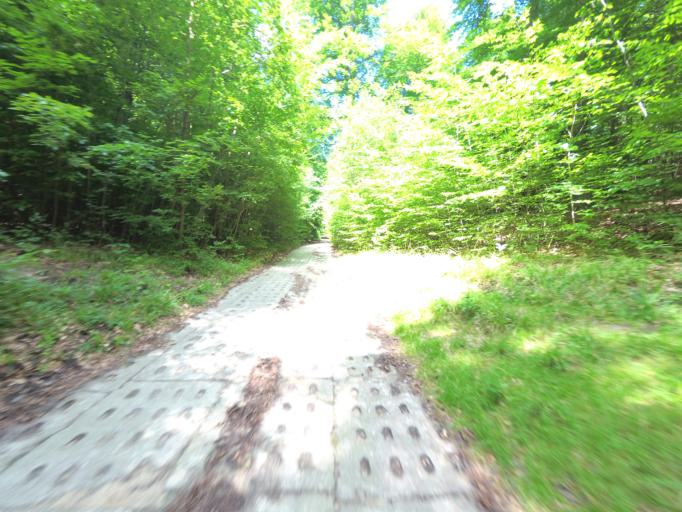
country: PL
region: Pomeranian Voivodeship
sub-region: Gdynia
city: Wielki Kack
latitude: 54.4883
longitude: 18.5077
